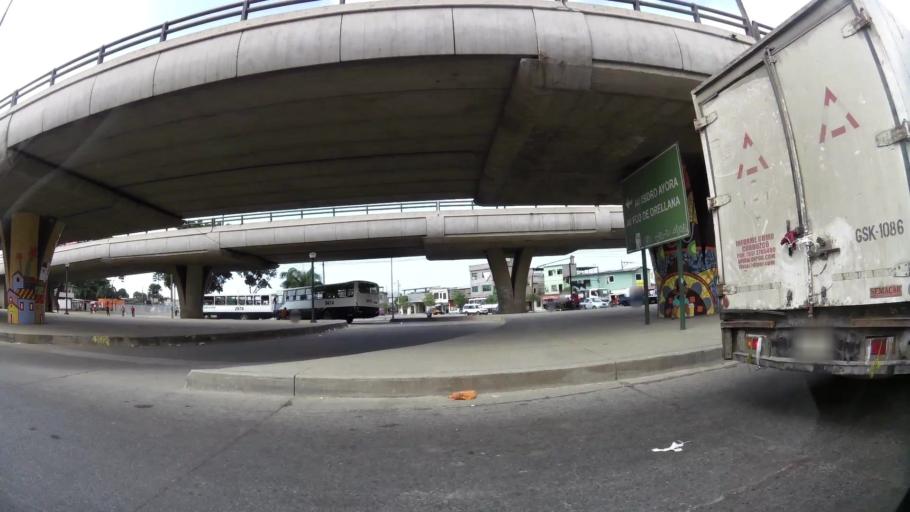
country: EC
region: Guayas
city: Santa Lucia
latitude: -2.0911
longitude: -79.9371
